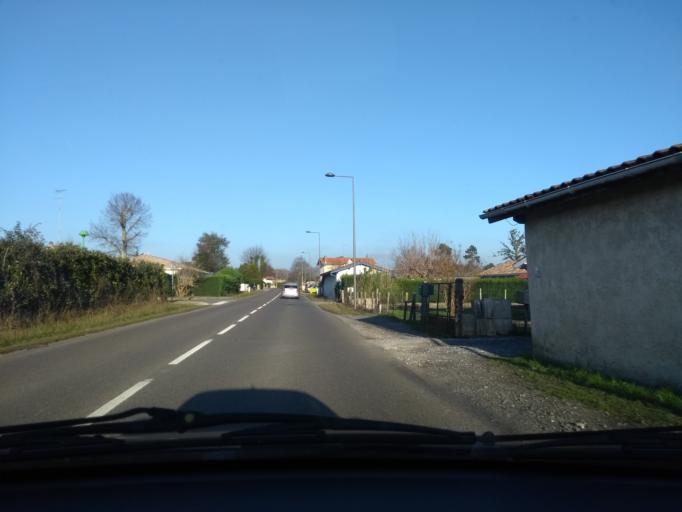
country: FR
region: Aquitaine
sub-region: Departement de la Gironde
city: Mios
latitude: 44.6076
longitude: -0.9316
